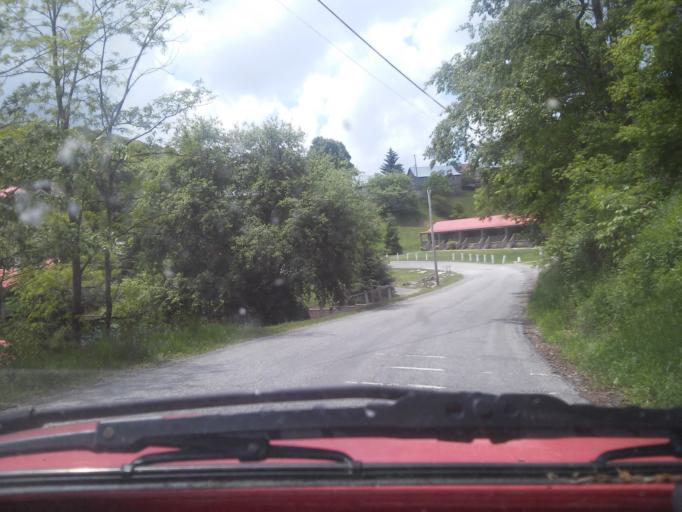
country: US
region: Virginia
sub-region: Giles County
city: Pembroke
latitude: 37.3566
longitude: -80.5373
